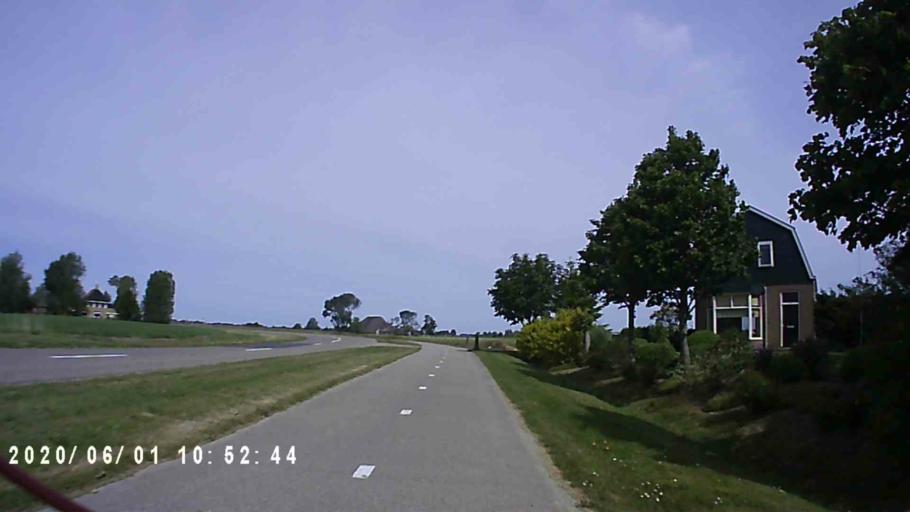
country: NL
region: Friesland
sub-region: Gemeente Franekeradeel
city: Franeker
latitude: 53.2005
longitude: 5.5167
